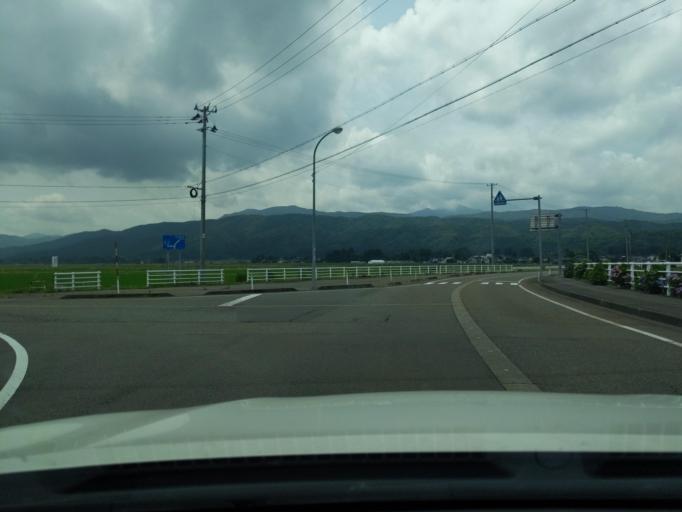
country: JP
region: Niigata
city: Kashiwazaki
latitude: 37.3302
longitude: 138.5754
